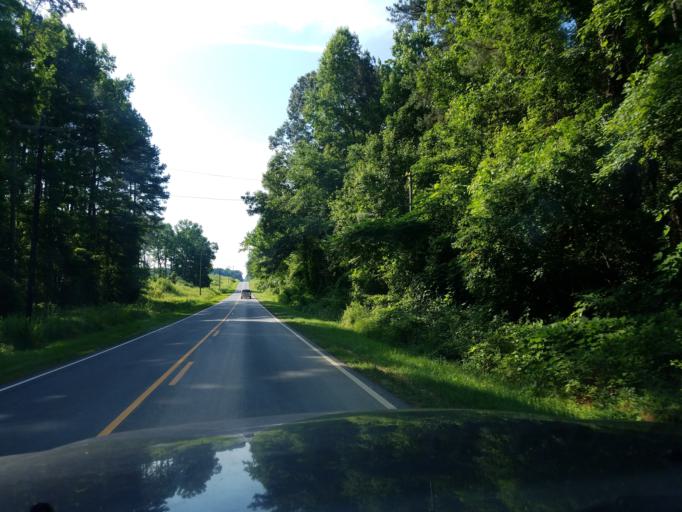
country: US
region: North Carolina
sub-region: Granville County
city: Butner
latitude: 36.1725
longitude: -78.7927
